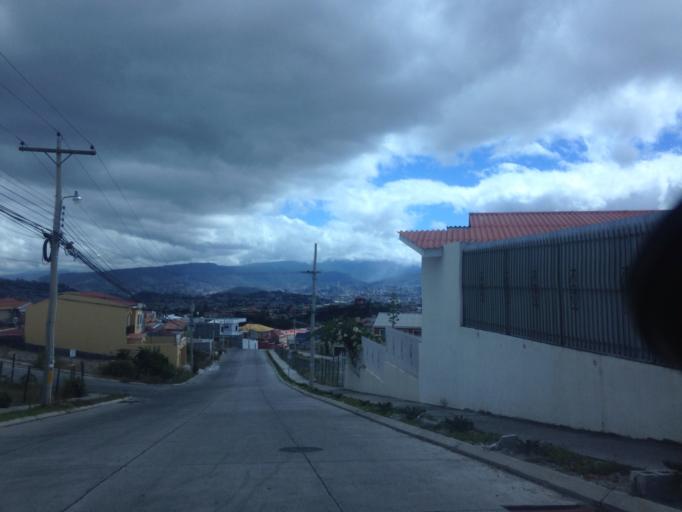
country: HN
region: Francisco Morazan
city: Yaguacire
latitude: 14.0500
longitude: -87.2450
